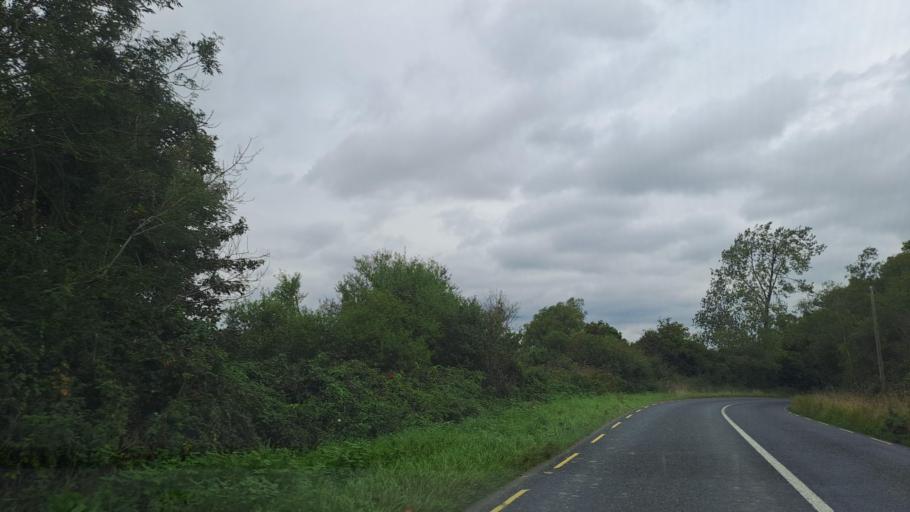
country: IE
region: Ulster
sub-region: An Cabhan
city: Bailieborough
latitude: 53.9668
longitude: -6.9154
